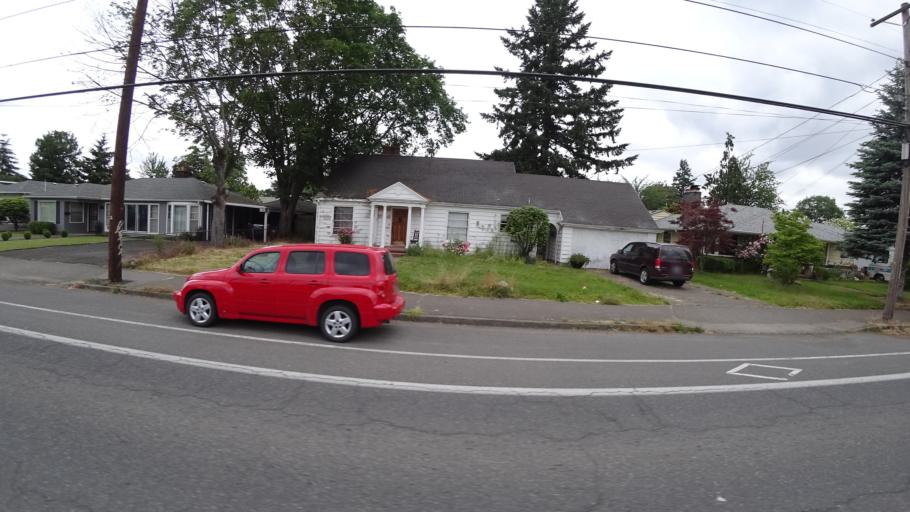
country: US
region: Oregon
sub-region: Multnomah County
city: Lents
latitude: 45.4687
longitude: -122.5813
